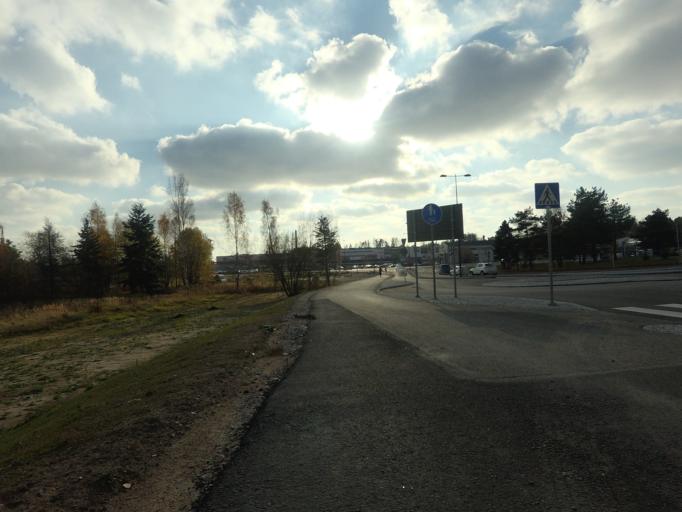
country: FI
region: Uusimaa
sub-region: Helsinki
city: Kauniainen
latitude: 60.1632
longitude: 24.7109
